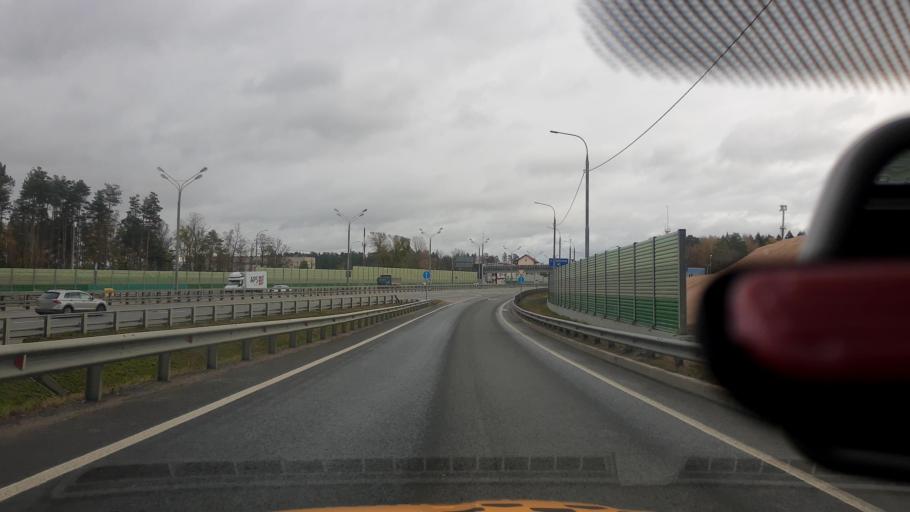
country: RU
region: Moskovskaya
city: Golitsyno
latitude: 55.6013
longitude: 36.9925
